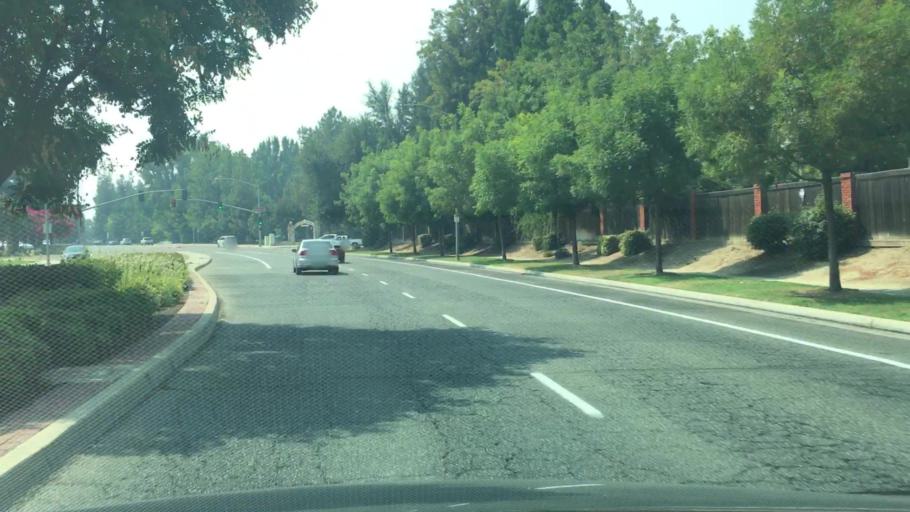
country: US
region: California
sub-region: Fresno County
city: Clovis
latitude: 36.8458
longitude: -119.7021
